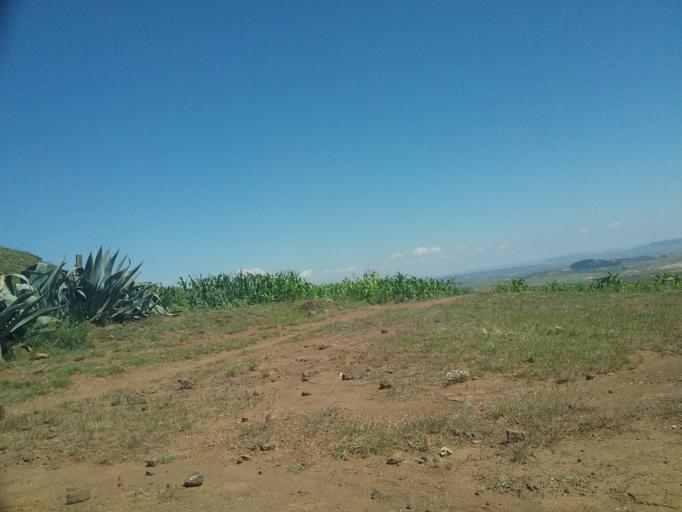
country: LS
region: Berea
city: Teyateyaneng
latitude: -29.2186
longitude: 27.8666
